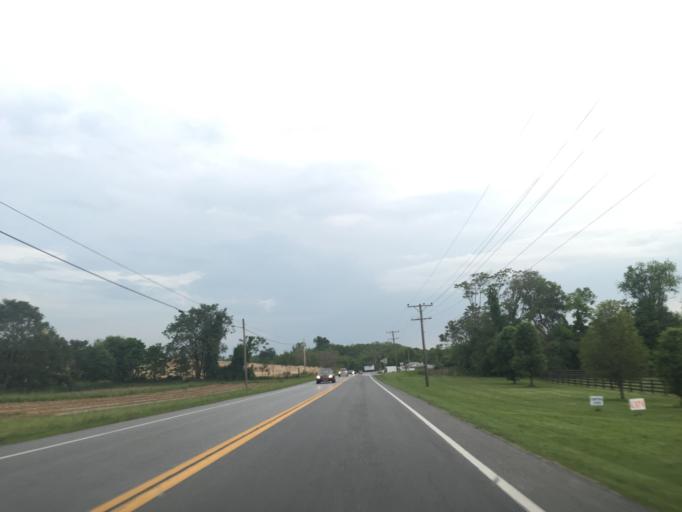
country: US
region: West Virginia
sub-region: Jefferson County
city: Charles Town
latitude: 39.2404
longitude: -77.8975
